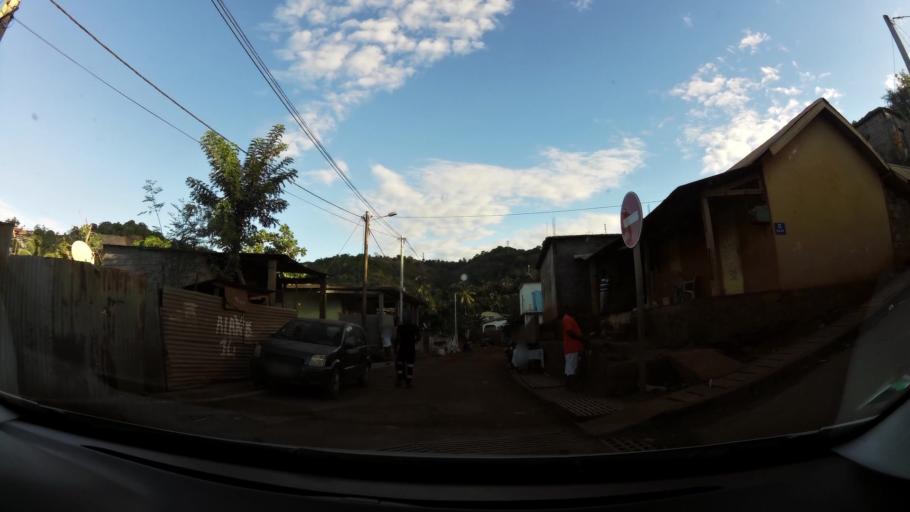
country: YT
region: Koungou
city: Koungou
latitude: -12.7397
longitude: 45.2045
